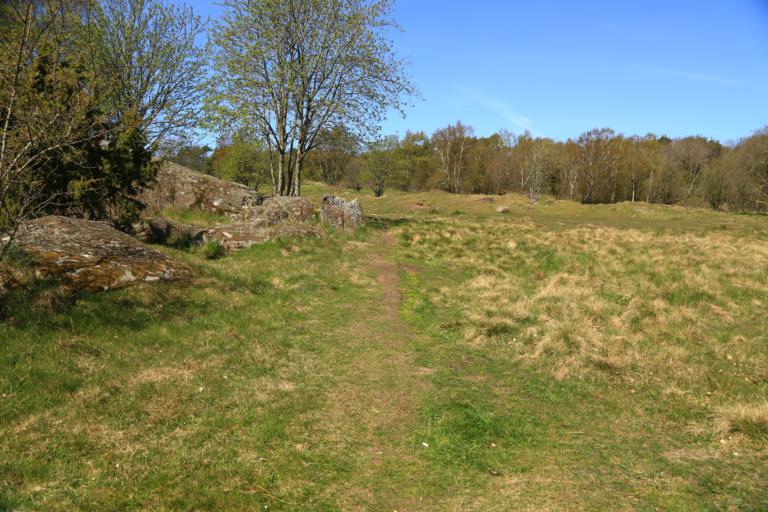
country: SE
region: Halland
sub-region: Varbergs Kommun
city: Traslovslage
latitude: 57.0912
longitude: 12.2753
